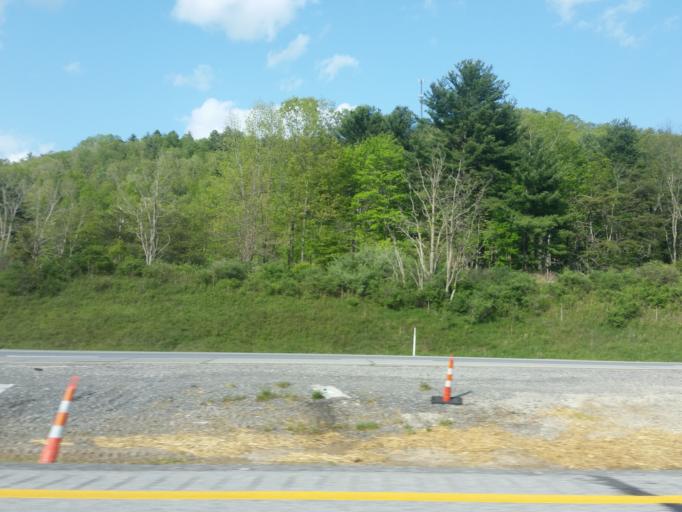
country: US
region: West Virginia
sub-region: Mercer County
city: Athens
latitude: 37.4847
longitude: -81.0780
